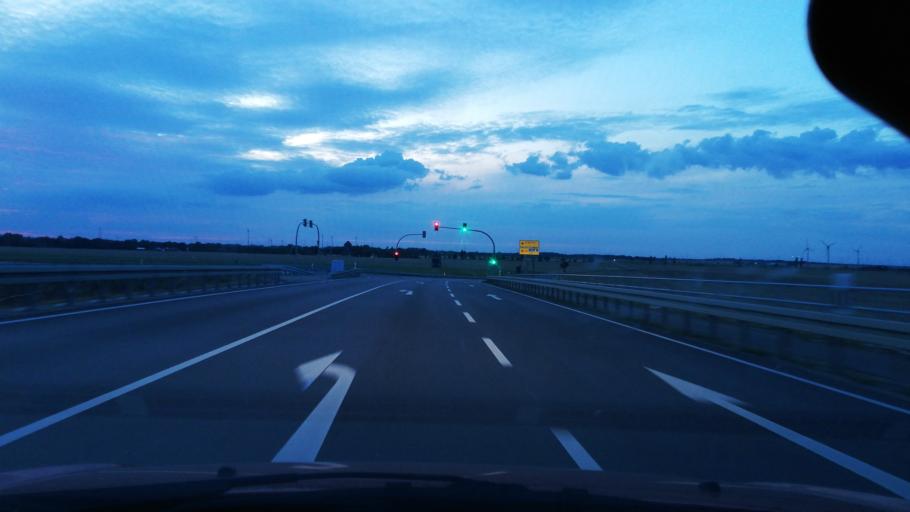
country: DE
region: Saxony-Anhalt
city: Landsberg
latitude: 51.5415
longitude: 12.1547
